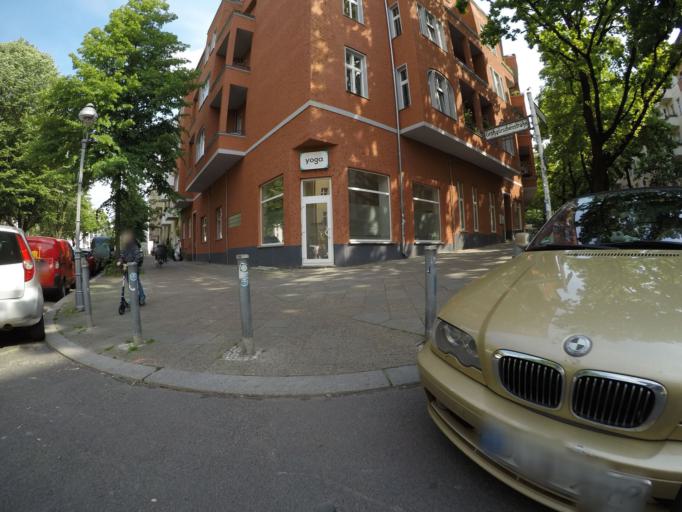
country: DE
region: Berlin
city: Berlin Schoeneberg
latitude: 52.4907
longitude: 13.3693
